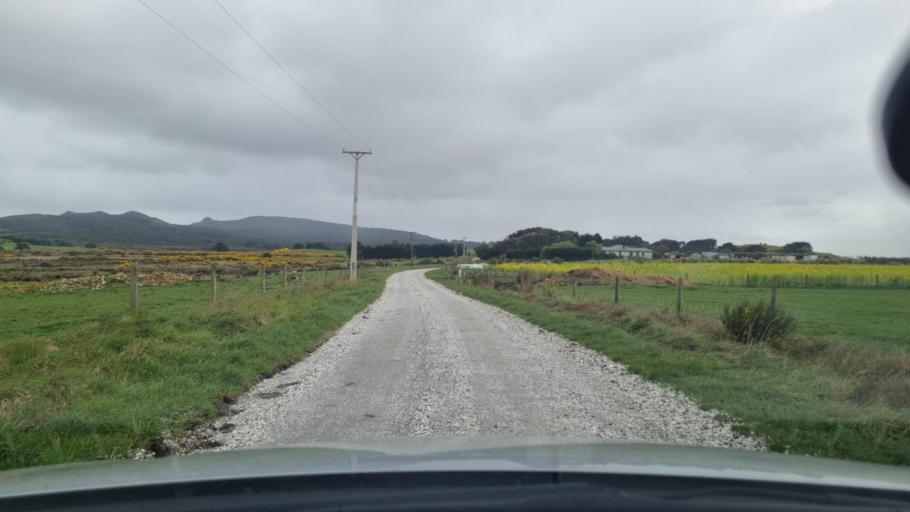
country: NZ
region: Southland
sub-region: Invercargill City
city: Bluff
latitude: -46.5443
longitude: 168.2971
